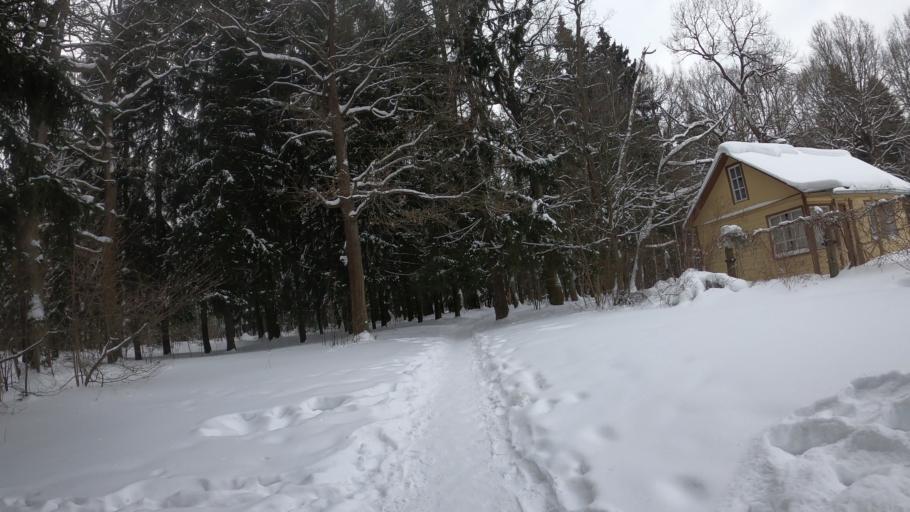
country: RU
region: Moskovskaya
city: Lugovaya
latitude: 56.0488
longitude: 37.4968
